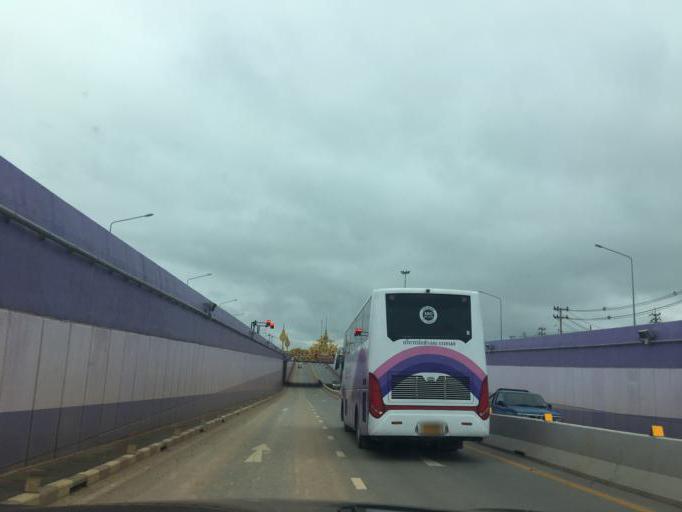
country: TH
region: Chiang Rai
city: Chiang Rai
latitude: 19.9567
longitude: 99.8781
